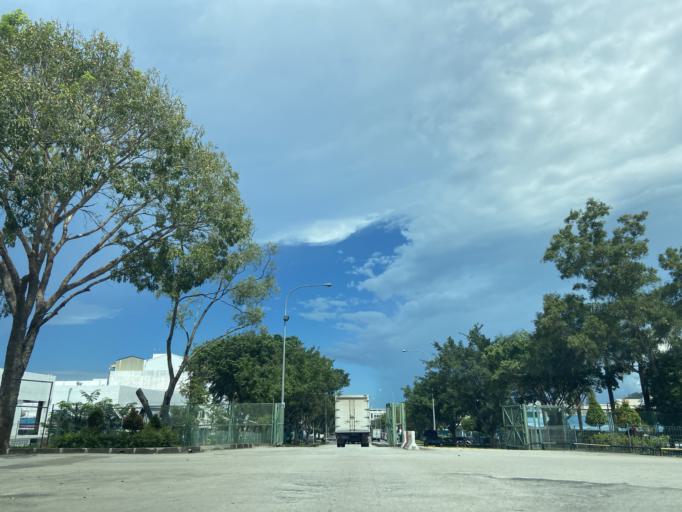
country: SG
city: Singapore
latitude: 1.0649
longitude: 104.0315
